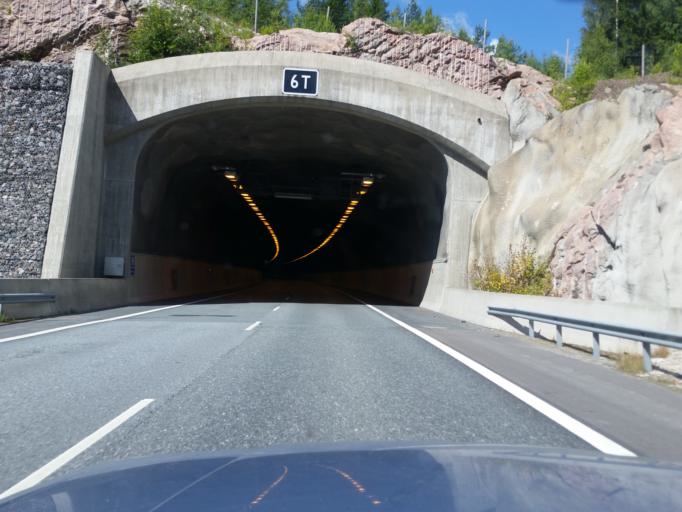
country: FI
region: Uusimaa
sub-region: Helsinki
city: Saukkola
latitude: 60.3242
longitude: 23.9548
